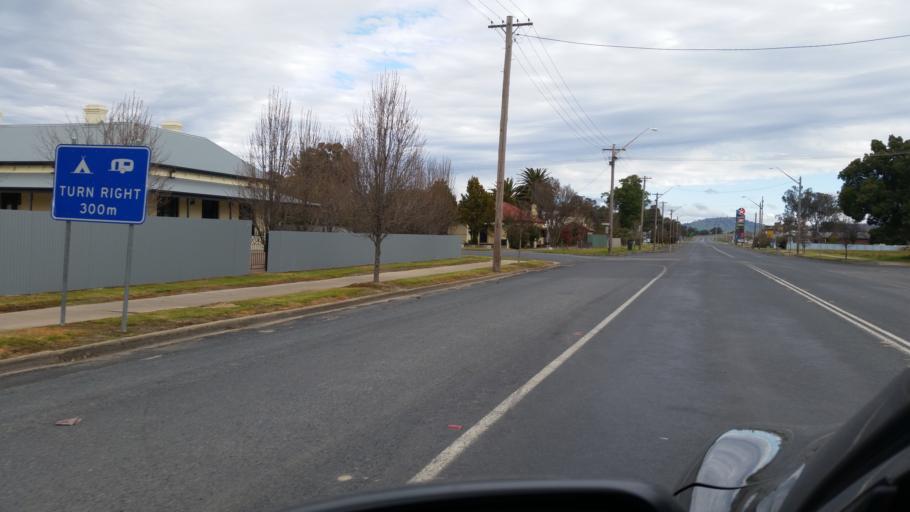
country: AU
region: New South Wales
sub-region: Greater Hume Shire
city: Holbrook
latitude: -35.7275
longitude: 147.3113
